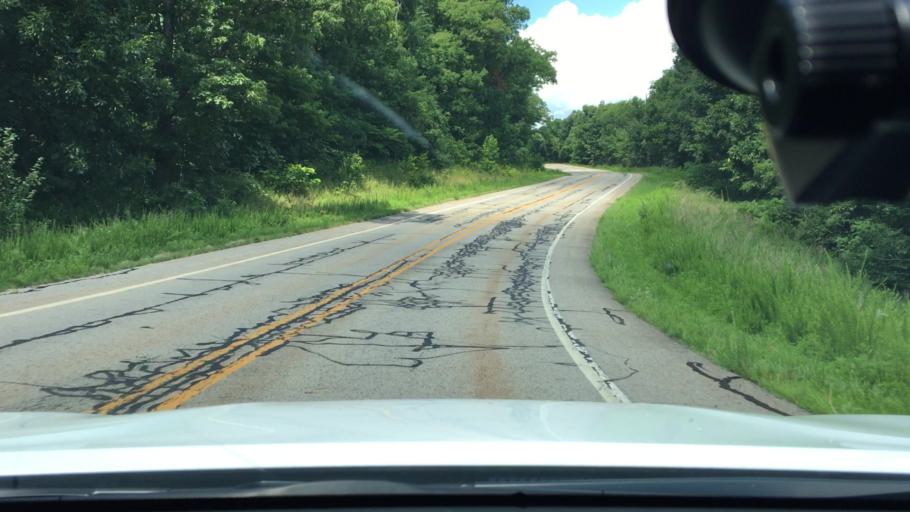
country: US
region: Arkansas
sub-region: Logan County
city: Paris
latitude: 35.1738
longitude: -93.6214
